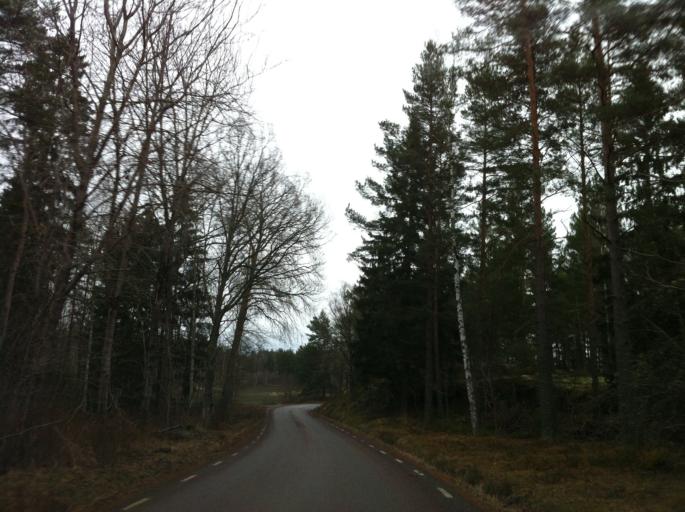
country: SE
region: Kalmar
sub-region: Vasterviks Kommun
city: Forserum
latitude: 57.9265
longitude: 16.5394
